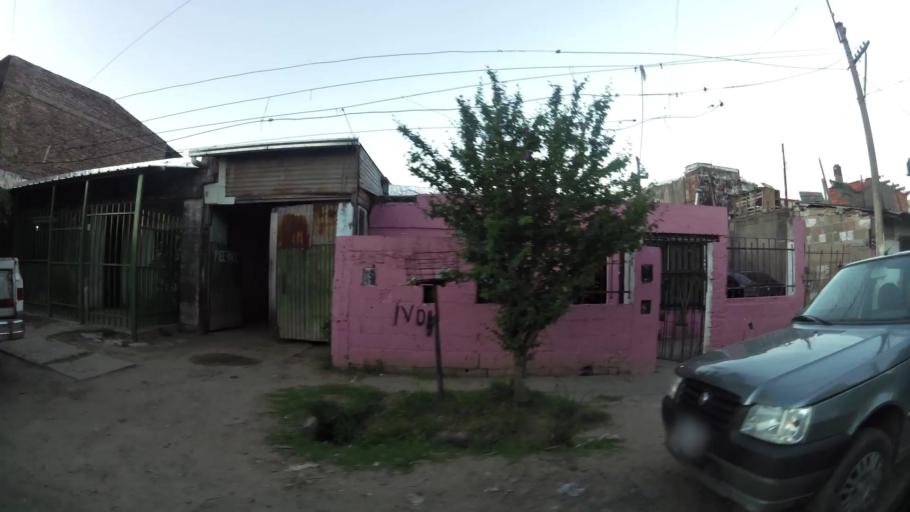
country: AR
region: Santa Fe
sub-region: Departamento de Rosario
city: Rosario
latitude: -32.9734
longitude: -60.6883
